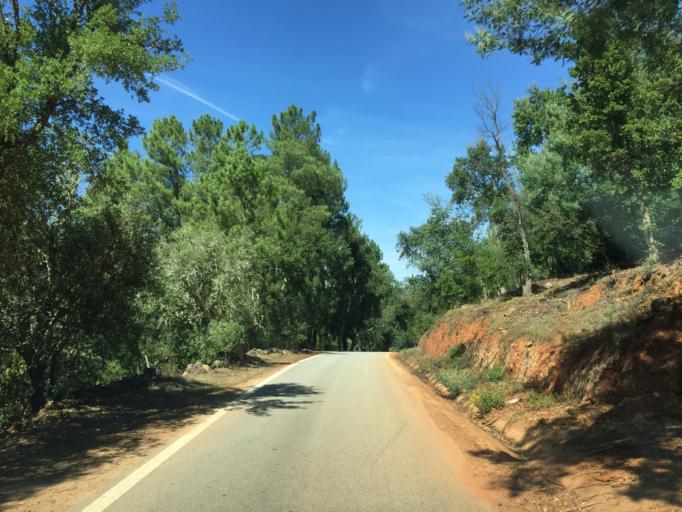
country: PT
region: Portalegre
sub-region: Marvao
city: Marvao
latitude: 39.3752
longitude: -7.3835
